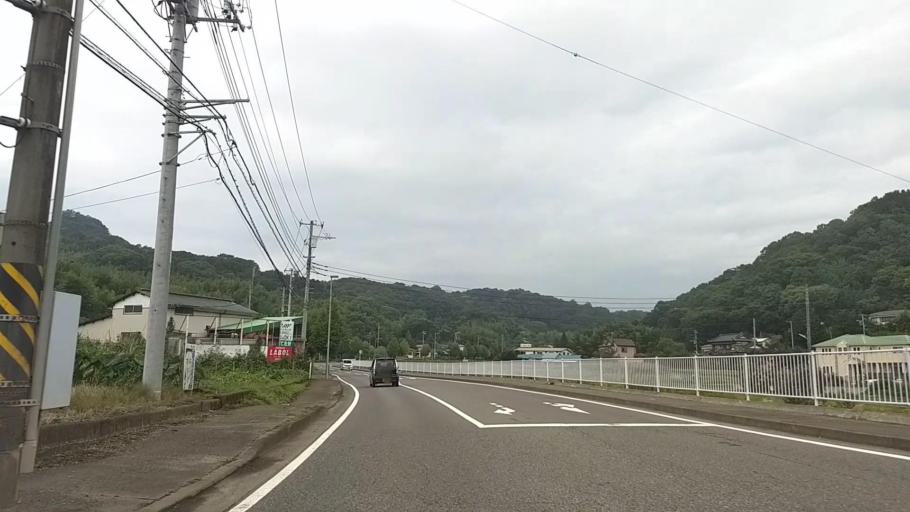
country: JP
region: Kanagawa
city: Hadano
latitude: 35.3325
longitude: 139.2049
